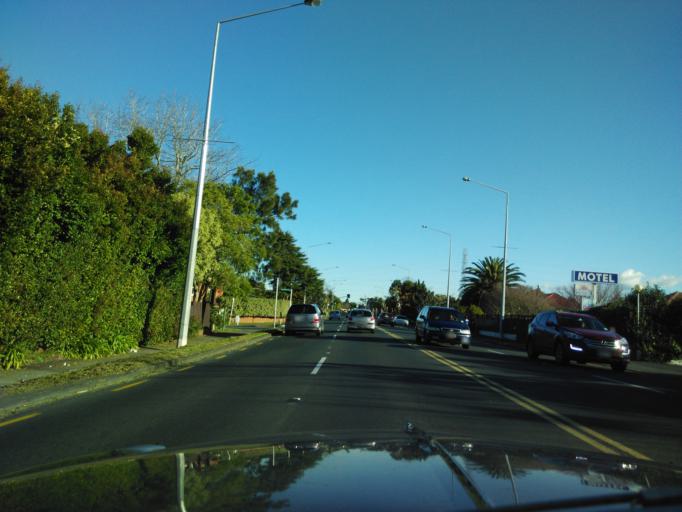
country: NZ
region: Auckland
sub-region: Auckland
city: Rosebank
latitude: -36.8611
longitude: 174.6500
